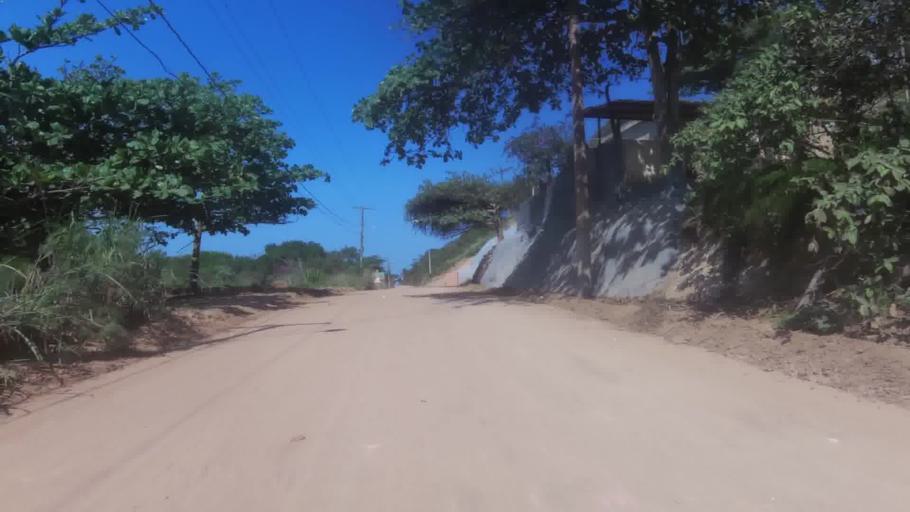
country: BR
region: Espirito Santo
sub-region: Marataizes
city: Marataizes
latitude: -21.0838
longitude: -40.8433
